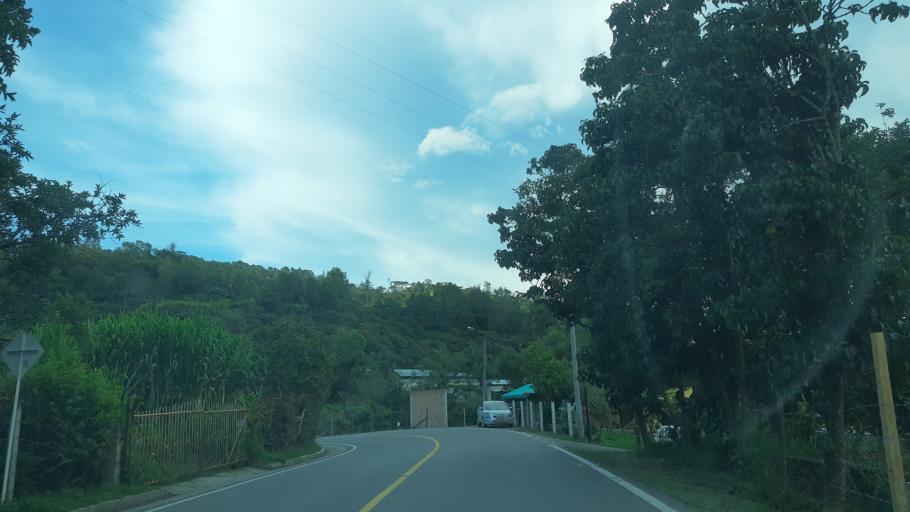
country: CO
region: Boyaca
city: Guateque
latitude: 5.0122
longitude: -73.4586
